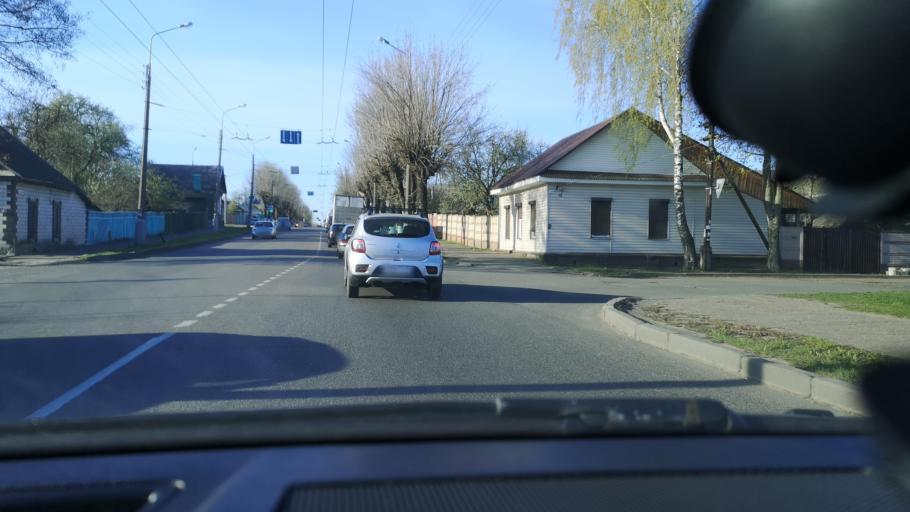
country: BY
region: Gomel
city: Gomel
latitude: 52.4301
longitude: 30.9751
